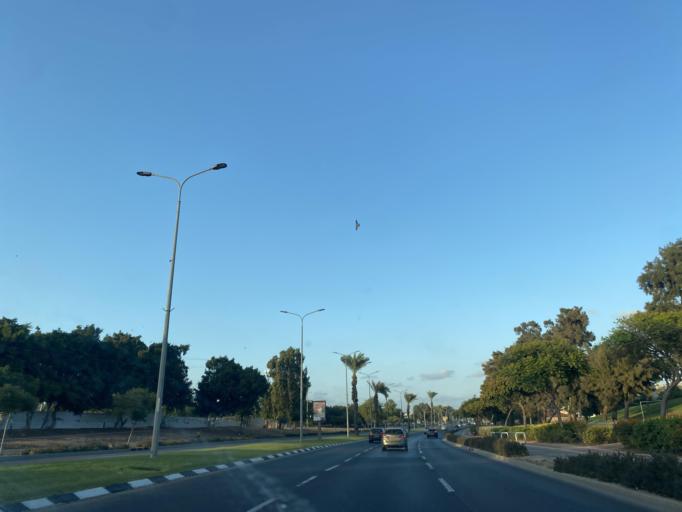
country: IL
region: Southern District
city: Ashdod
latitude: 31.8015
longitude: 34.6564
